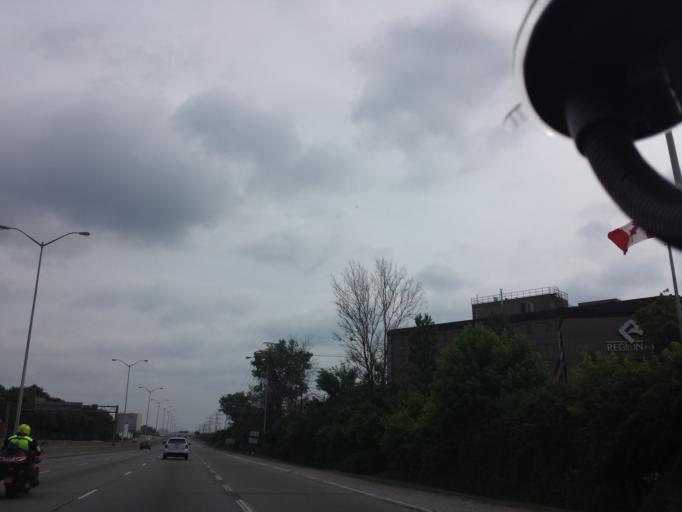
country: CA
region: Ontario
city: Ottawa
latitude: 45.3725
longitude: -75.7521
